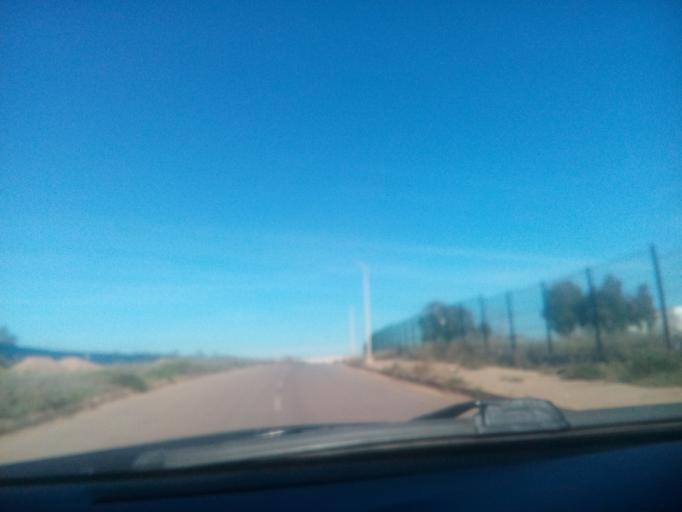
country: DZ
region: Oran
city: Bir el Djir
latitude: 35.7302
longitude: -0.5415
